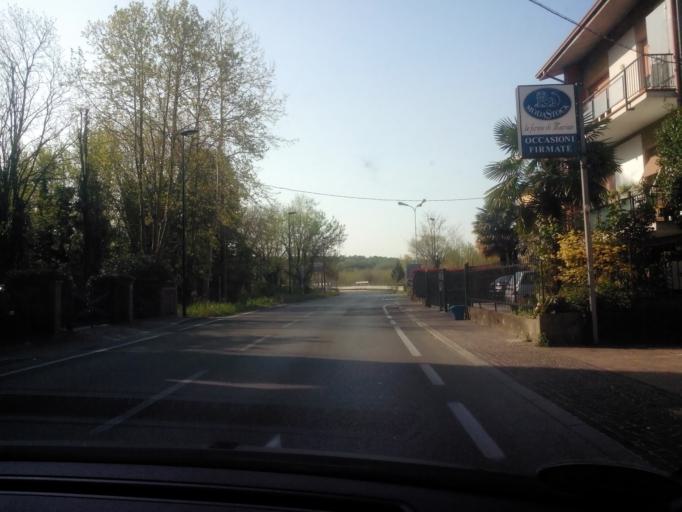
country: IT
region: Lombardy
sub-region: Provincia di Brescia
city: Padenghe sul Garda
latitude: 45.4912
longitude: 10.5132
